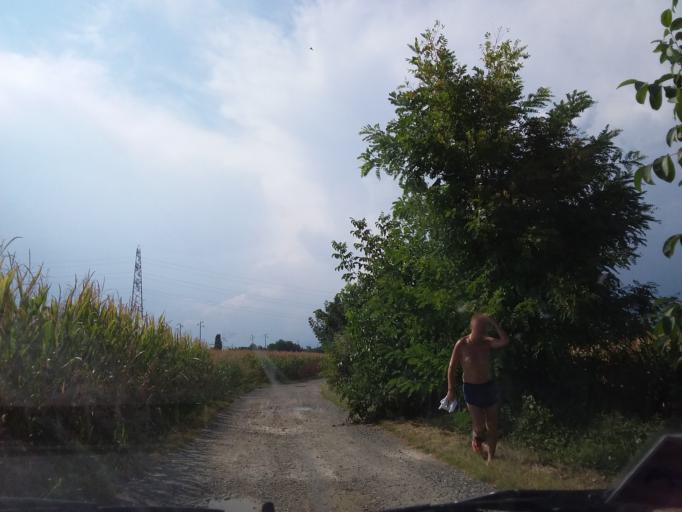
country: IT
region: Piedmont
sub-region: Provincia di Torino
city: Pianezza
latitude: 45.0869
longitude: 7.5409
